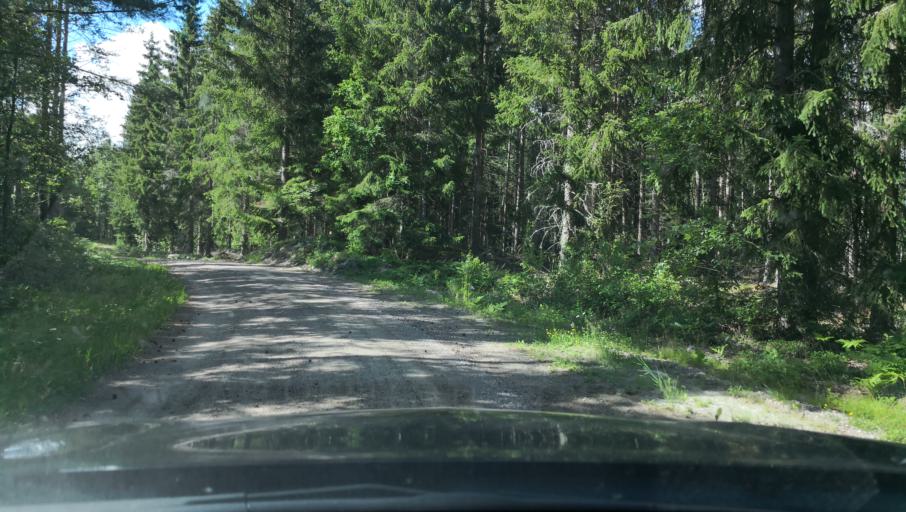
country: SE
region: Vaestmanland
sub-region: Arboga Kommun
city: Tyringe
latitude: 59.3281
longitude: 16.0307
